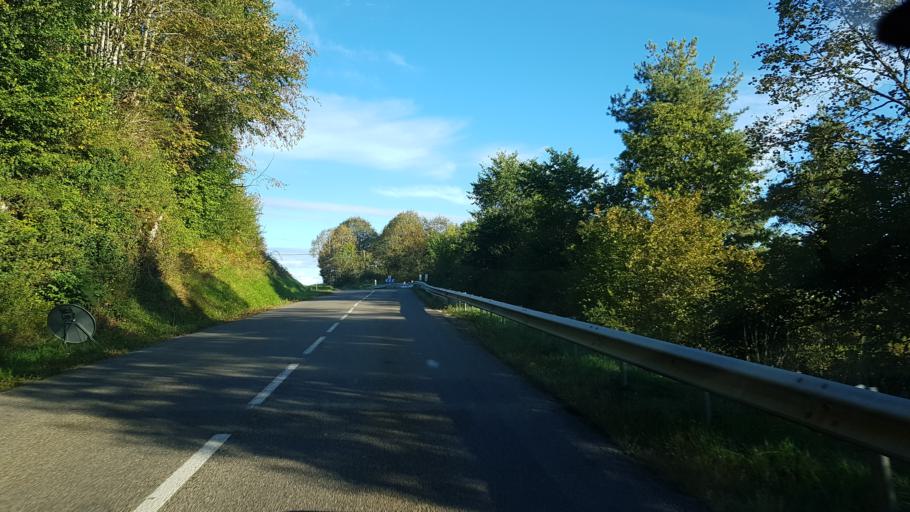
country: FR
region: Franche-Comte
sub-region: Departement du Jura
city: Lons-le-Saunier
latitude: 46.6360
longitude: 5.5406
